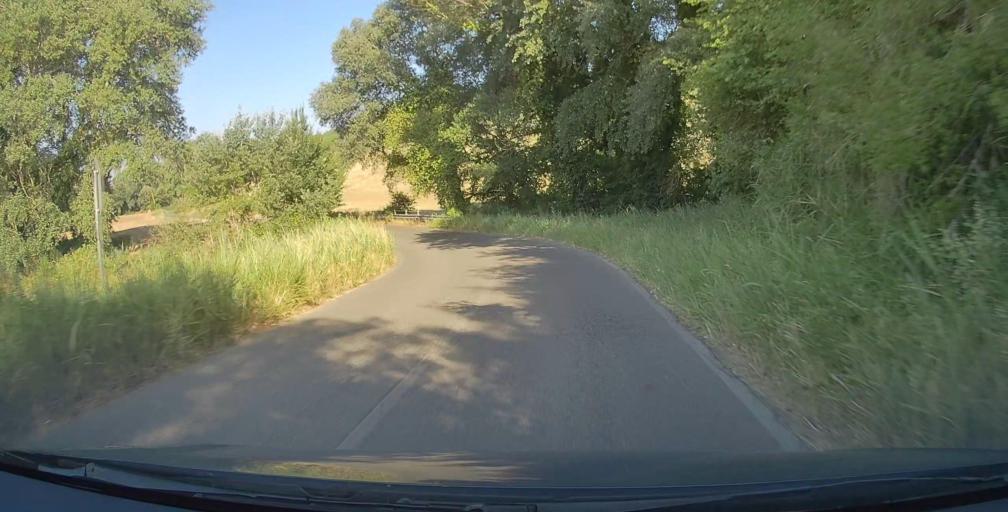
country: IT
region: Umbria
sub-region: Provincia di Terni
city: Otricoli
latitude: 42.3994
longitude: 12.4875
